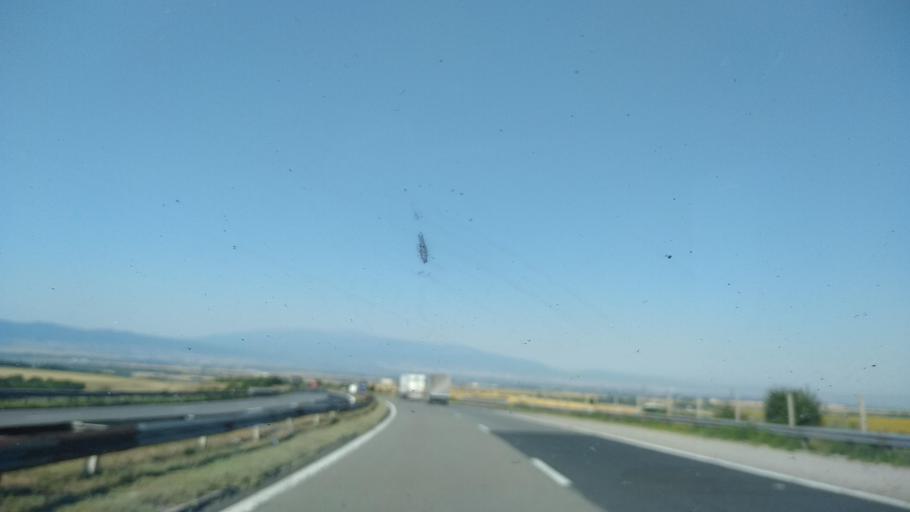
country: BG
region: Sofiya
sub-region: Obshtina Gorna Malina
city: Gorna Malina
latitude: 42.7509
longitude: 23.6821
